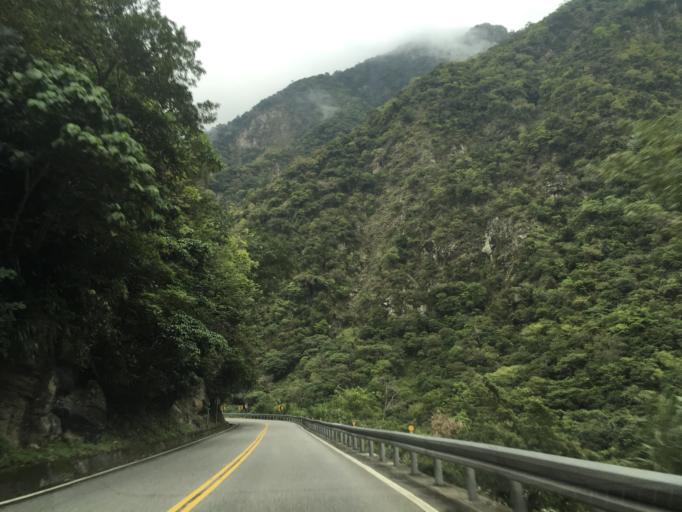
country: TW
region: Taiwan
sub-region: Hualien
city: Hualian
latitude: 24.1758
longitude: 121.5874
